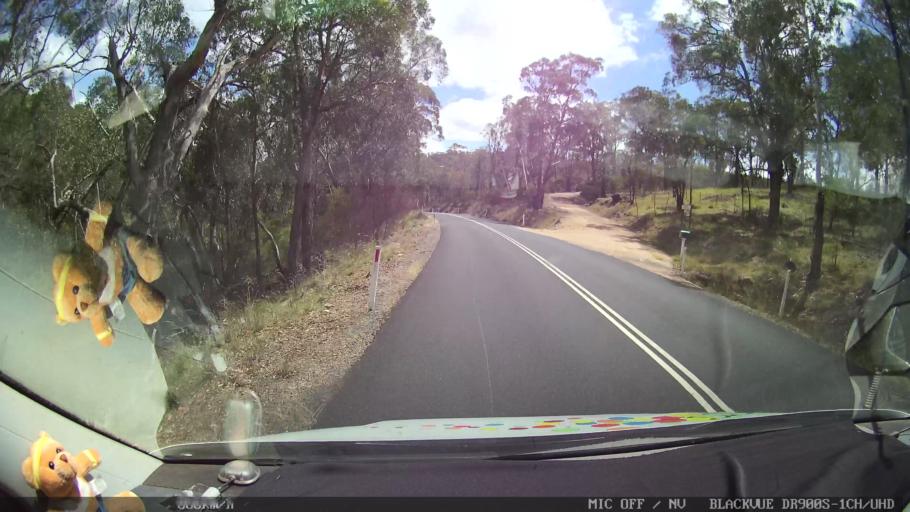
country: AU
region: New South Wales
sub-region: Glen Innes Severn
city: Glen Innes
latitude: -29.5655
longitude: 151.6689
